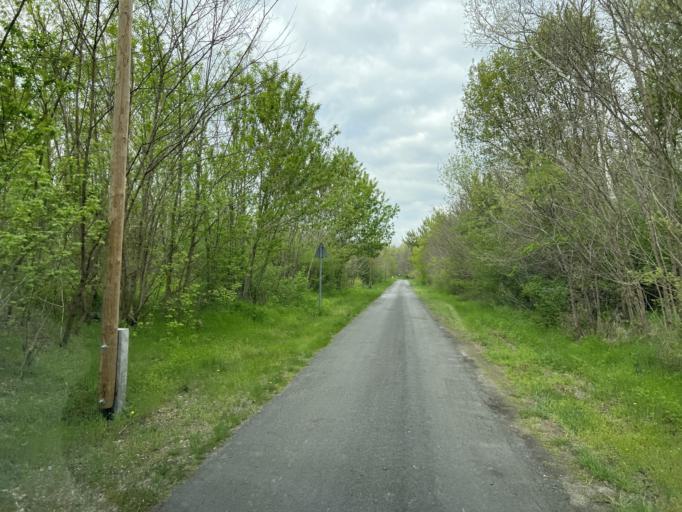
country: HU
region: Pest
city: Orkeny
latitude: 47.0439
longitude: 19.3514
